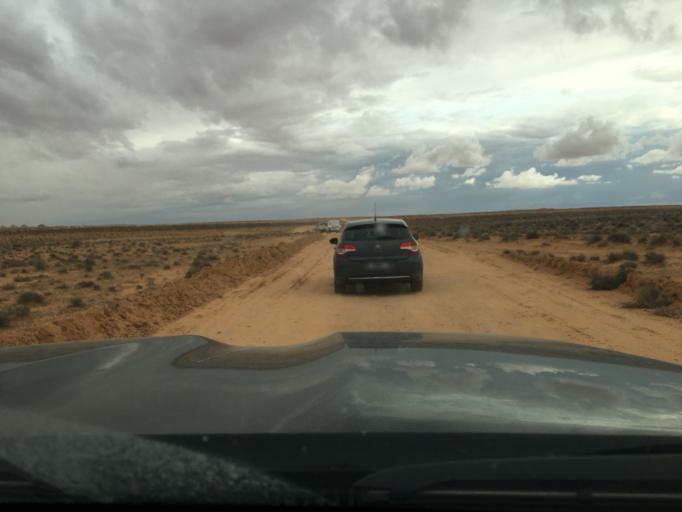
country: TN
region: Madanin
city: Medenine
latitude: 33.2627
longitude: 10.5718
